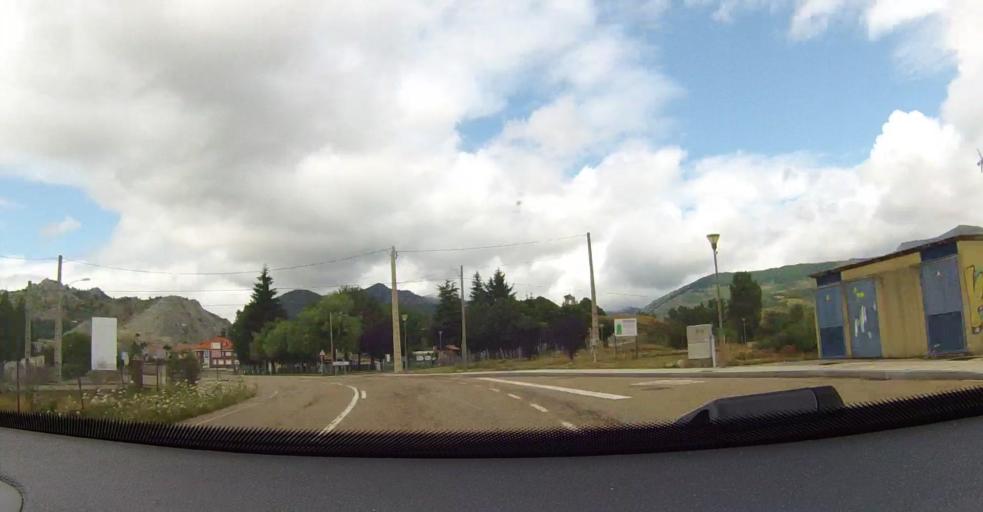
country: ES
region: Castille and Leon
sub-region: Provincia de Leon
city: Puebla de Lillo
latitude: 43.0030
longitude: -5.2671
